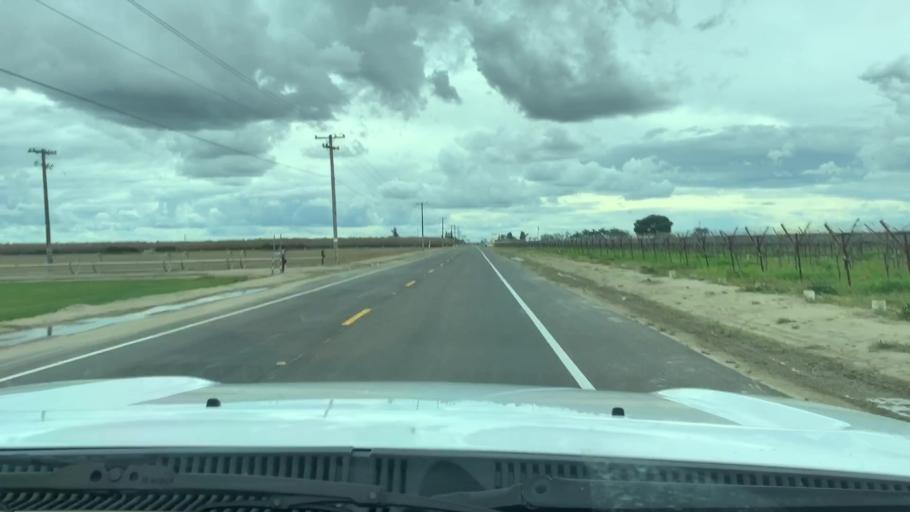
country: US
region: California
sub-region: Fresno County
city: Laton
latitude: 36.5079
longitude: -119.6830
